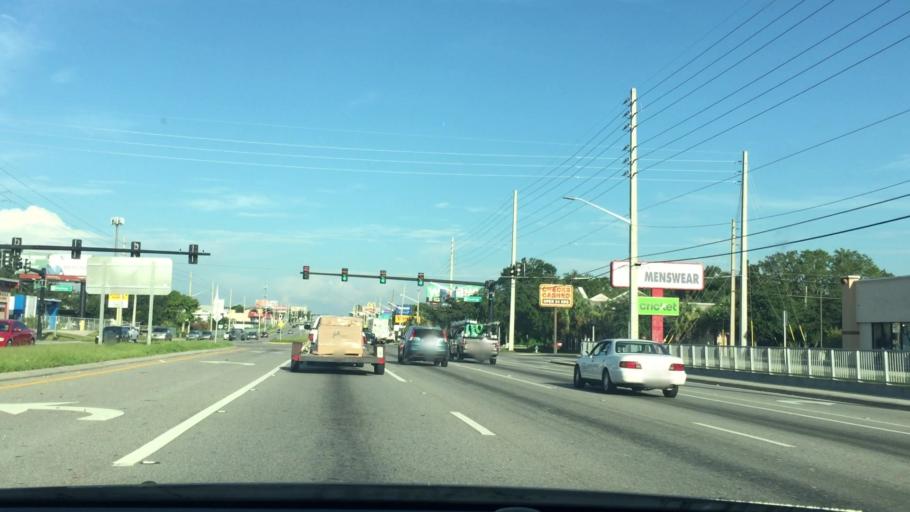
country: US
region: Florida
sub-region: Orange County
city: Pine Hills
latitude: 28.5525
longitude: -81.4589
